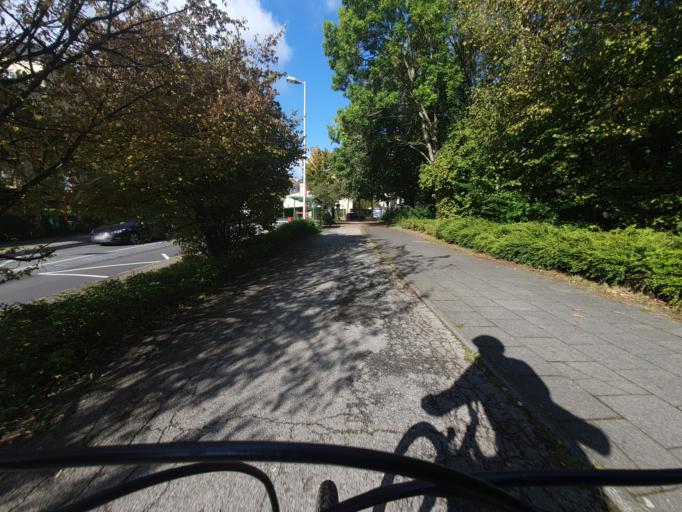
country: DE
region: North Rhine-Westphalia
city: Opladen
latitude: 51.0407
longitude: 7.0507
